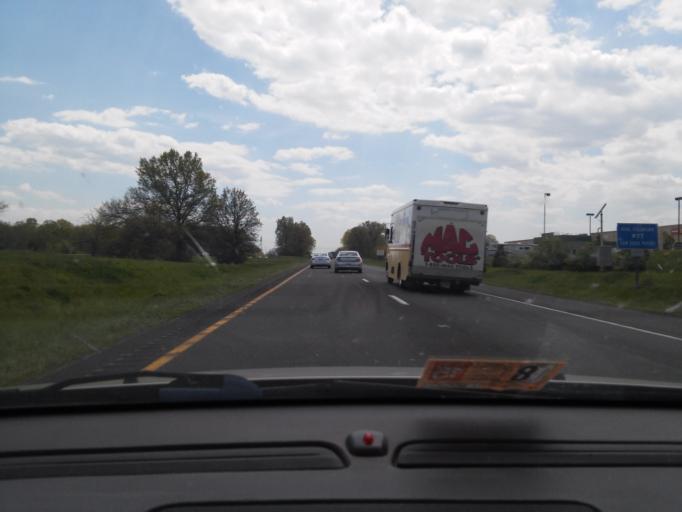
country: US
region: West Virginia
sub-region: Berkeley County
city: Inwood
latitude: 39.2840
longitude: -78.0883
